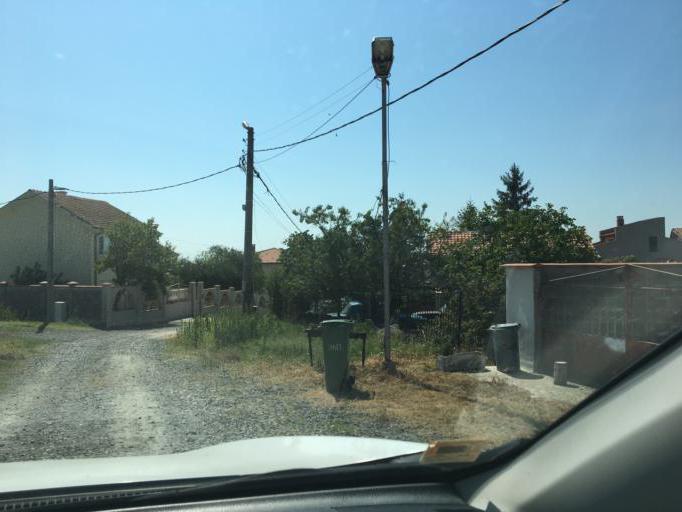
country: BG
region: Burgas
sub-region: Obshtina Kameno
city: Kameno
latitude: 42.6333
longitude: 27.3909
